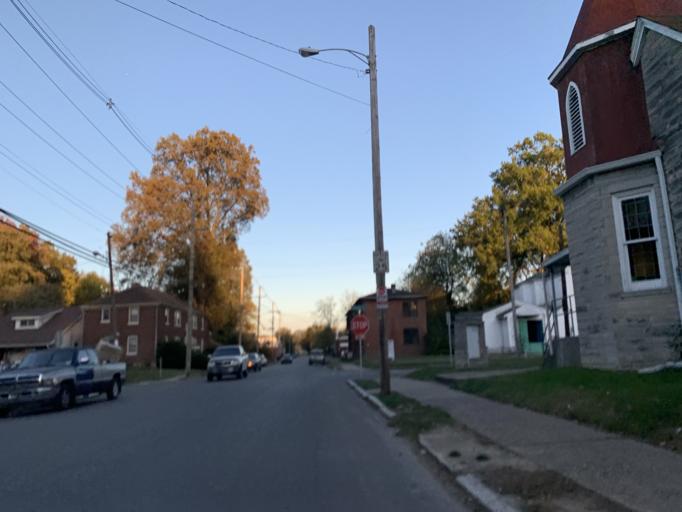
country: US
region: Kentucky
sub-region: Jefferson County
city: Shively
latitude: 38.2320
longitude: -85.8056
